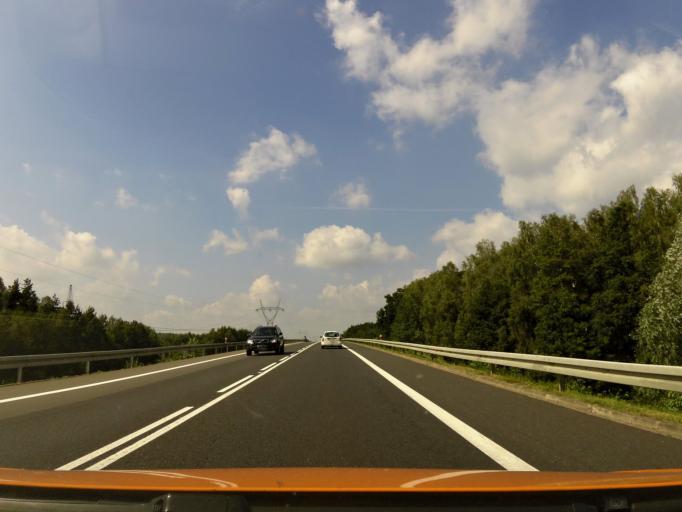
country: PL
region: West Pomeranian Voivodeship
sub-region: Powiat goleniowski
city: Goleniow
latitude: 53.5883
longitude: 14.8463
